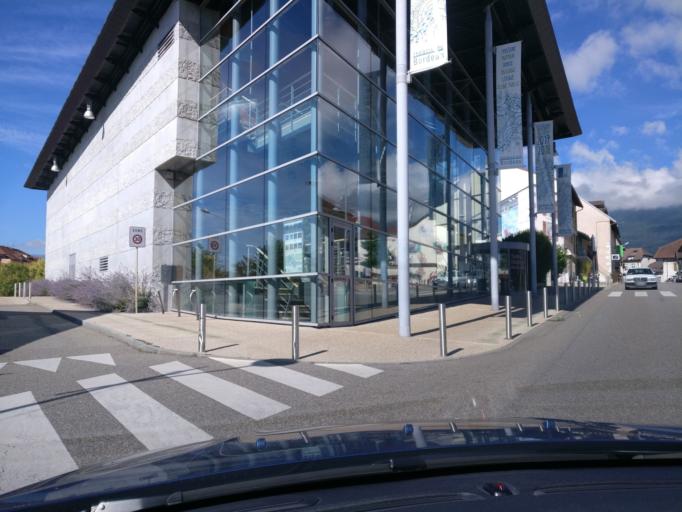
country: FR
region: Rhone-Alpes
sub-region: Departement de l'Ain
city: Saint-Genis-Pouilly
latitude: 46.2427
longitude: 6.0228
